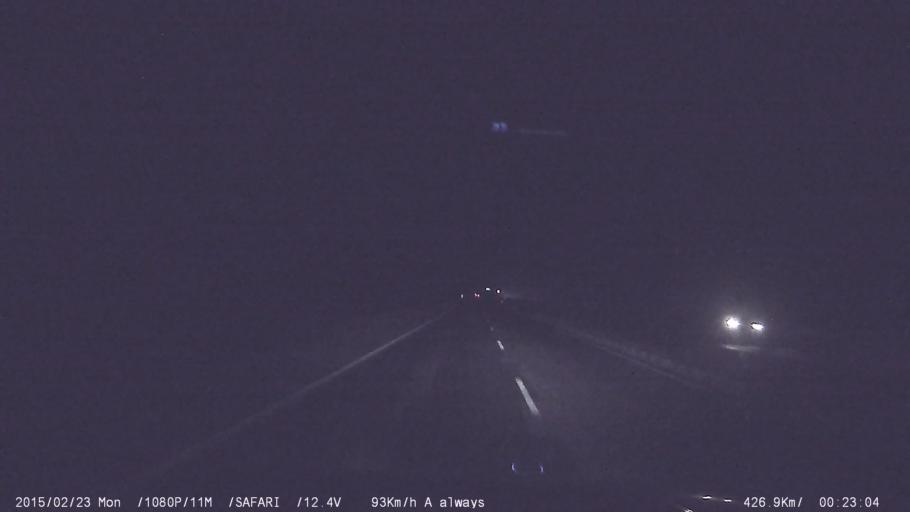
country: IN
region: Tamil Nadu
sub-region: Salem
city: Omalur
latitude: 11.9190
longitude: 78.0617
